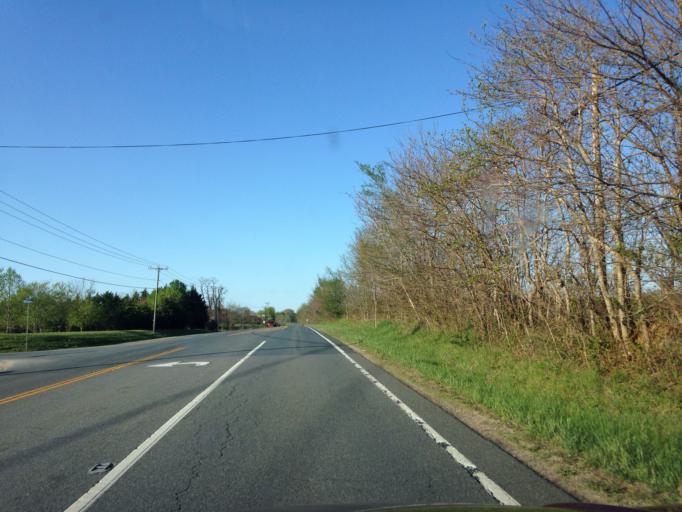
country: US
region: Virginia
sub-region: Loudoun County
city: Lovettsville
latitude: 39.2110
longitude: -77.6660
